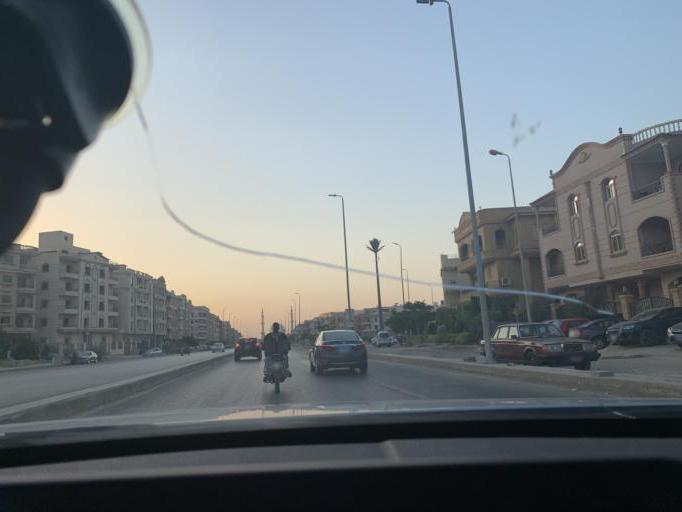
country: EG
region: Muhafazat al Qahirah
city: Cairo
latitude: 30.0006
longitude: 31.4624
